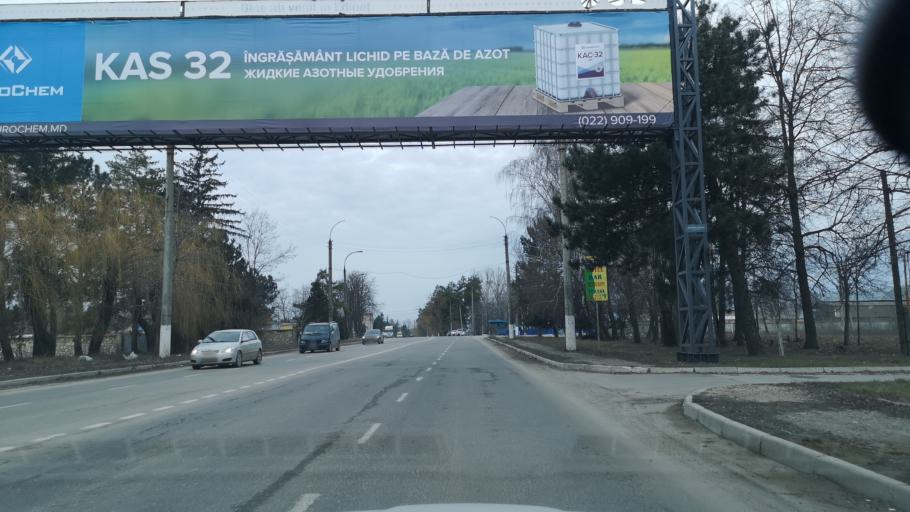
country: MD
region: Raionul Edinet
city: Edinet
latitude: 48.1602
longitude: 27.3285
